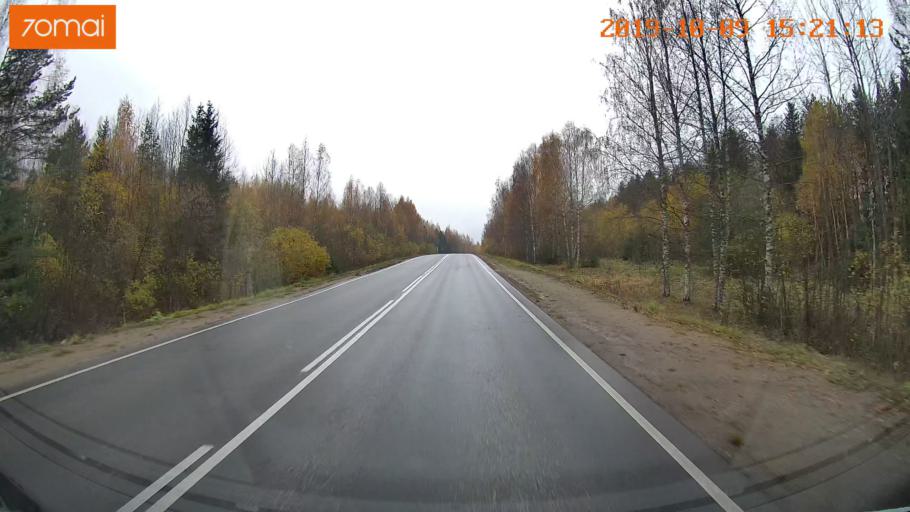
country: RU
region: Kostroma
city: Susanino
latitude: 58.0558
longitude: 41.5237
